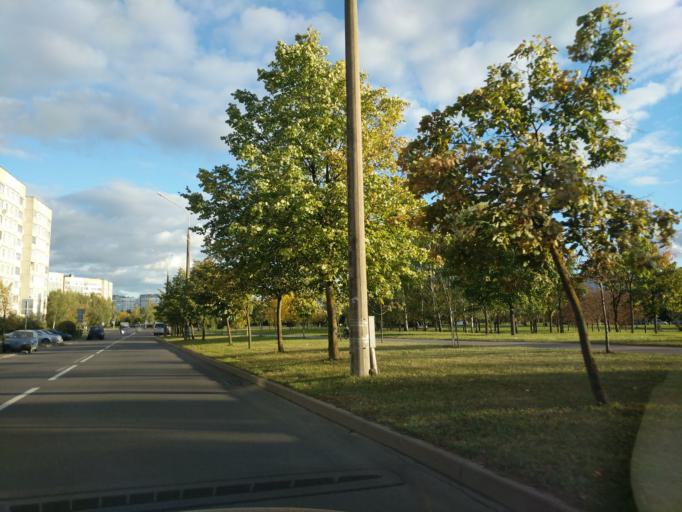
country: BY
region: Minsk
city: Malinovka
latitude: 53.8585
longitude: 27.4536
